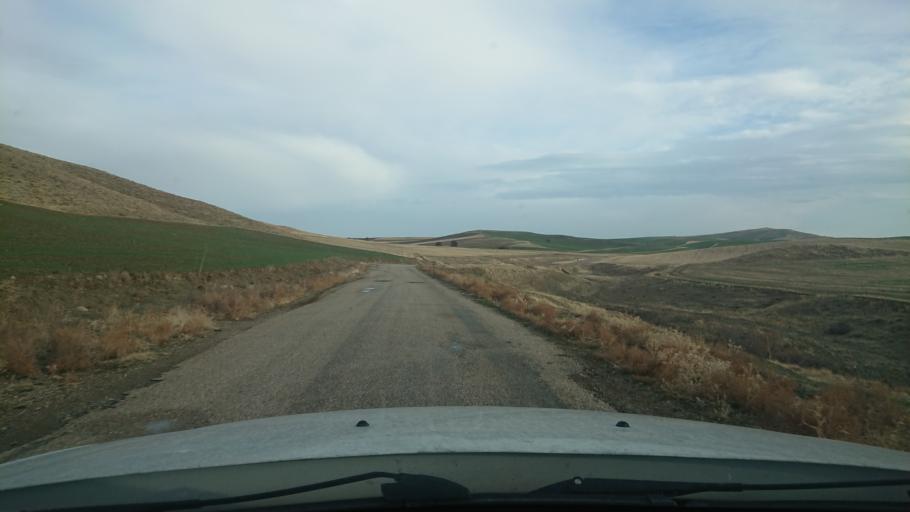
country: TR
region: Aksaray
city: Acipinar
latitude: 38.6413
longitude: 33.8081
